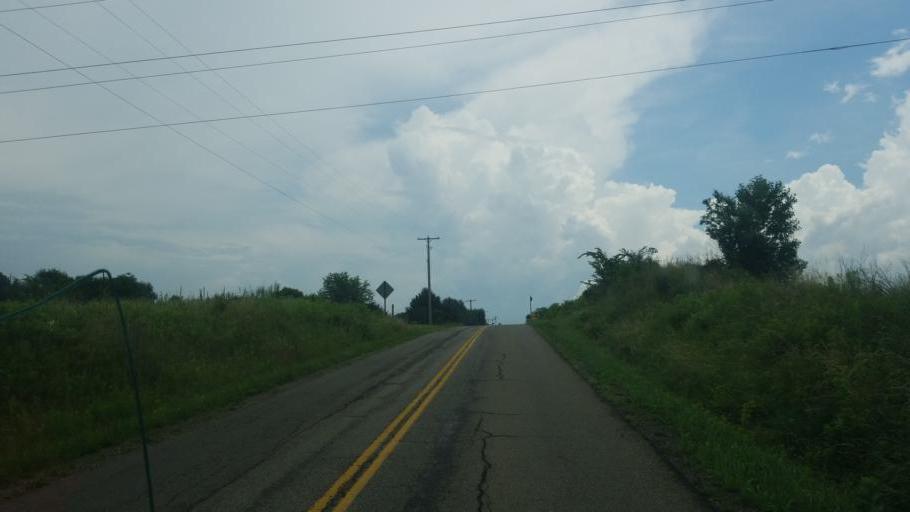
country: US
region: Ohio
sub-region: Summit County
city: Clinton
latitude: 40.8949
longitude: -81.6532
